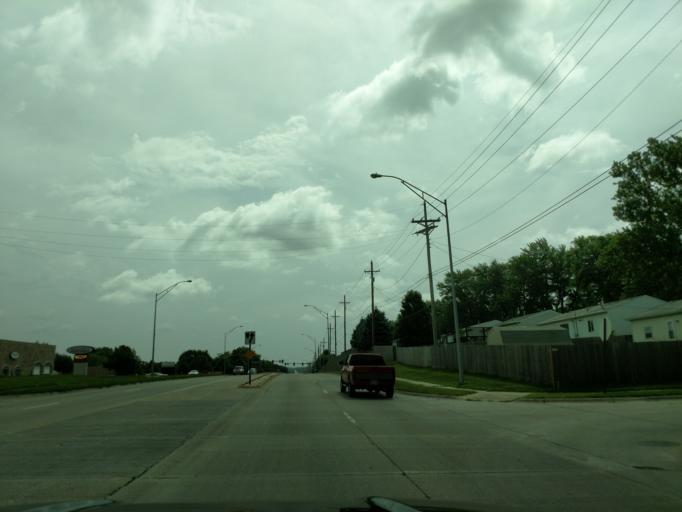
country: US
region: Nebraska
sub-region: Sarpy County
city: La Vista
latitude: 41.1908
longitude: -96.0369
